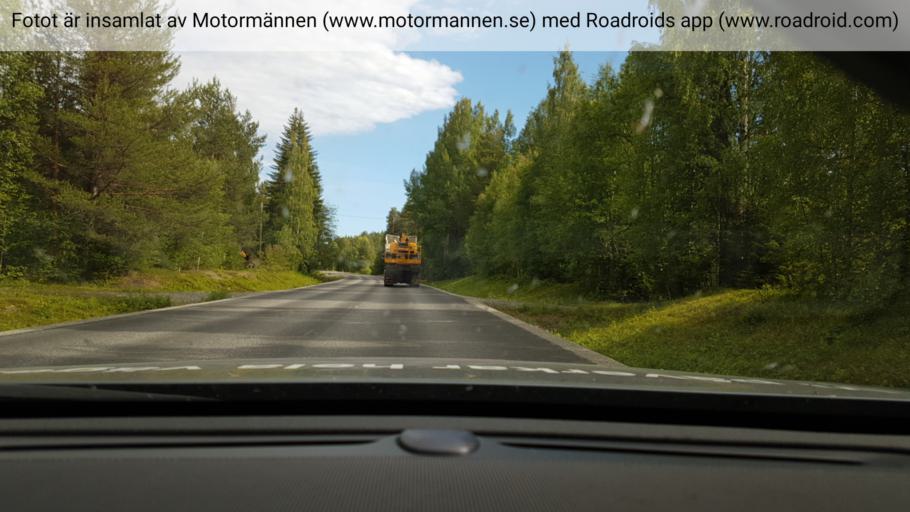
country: SE
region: Vaesterbotten
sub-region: Lycksele Kommun
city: Soderfors
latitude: 64.8578
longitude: 17.9342
